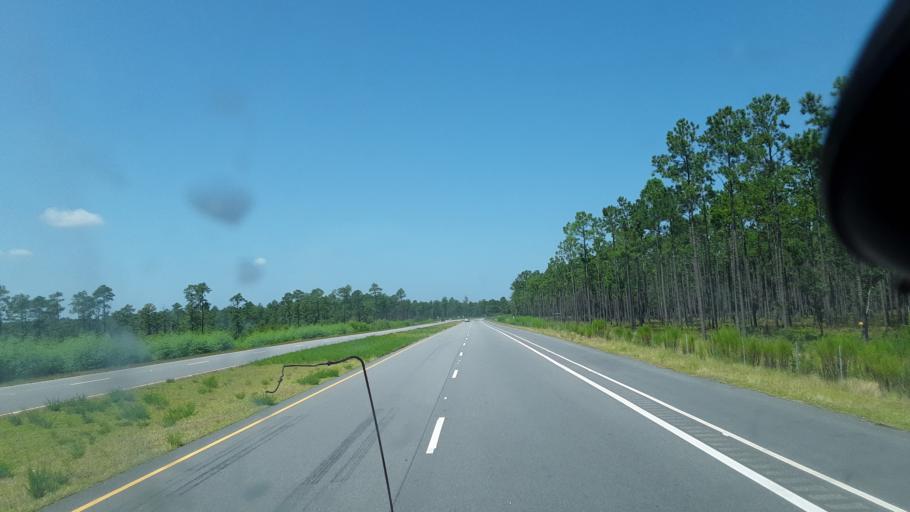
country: US
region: South Carolina
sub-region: Horry County
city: Forestbrook
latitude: 33.8041
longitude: -78.8880
